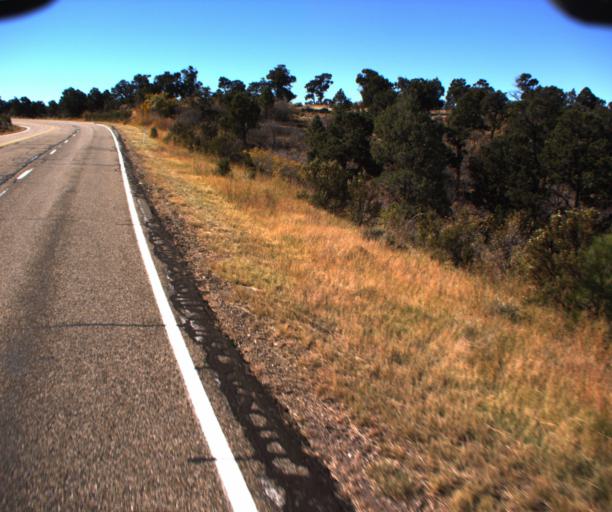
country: US
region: Arizona
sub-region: Coconino County
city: Fredonia
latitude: 36.8003
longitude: -112.2538
